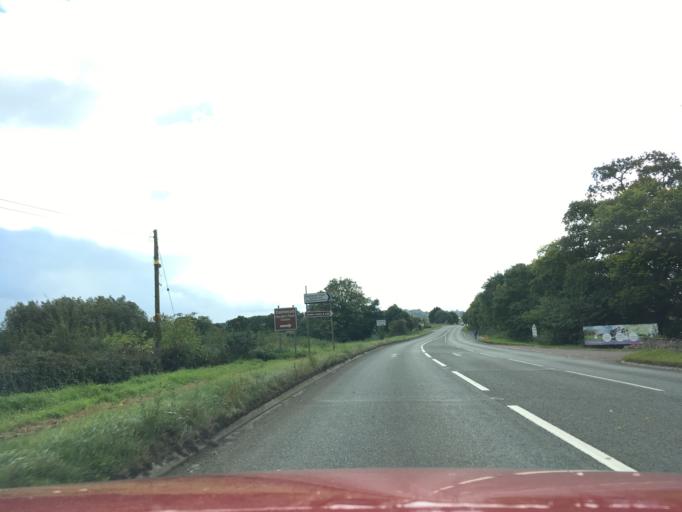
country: GB
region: England
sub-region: South Gloucestershire
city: Falfield
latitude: 51.6264
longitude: -2.4644
